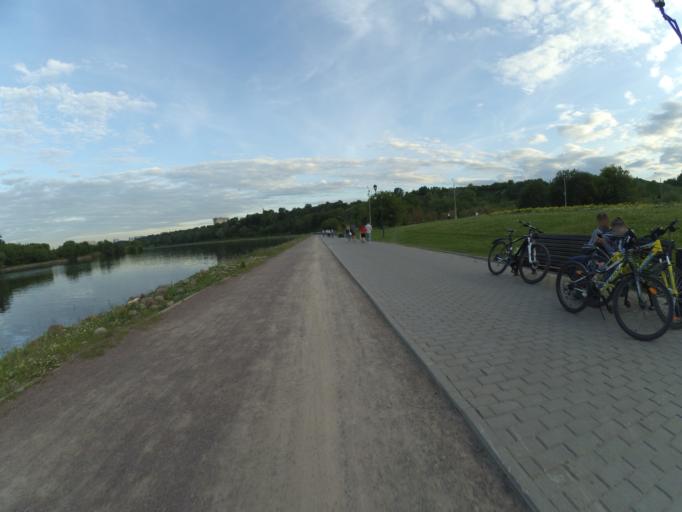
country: RU
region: Moscow
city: Kolomenskoye
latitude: 55.6575
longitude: 37.6700
